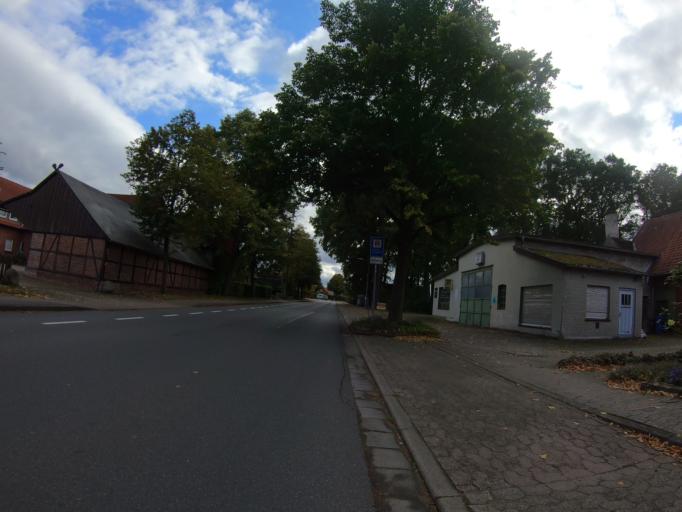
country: DE
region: Lower Saxony
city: Wasbuttel
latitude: 52.4160
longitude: 10.5910
